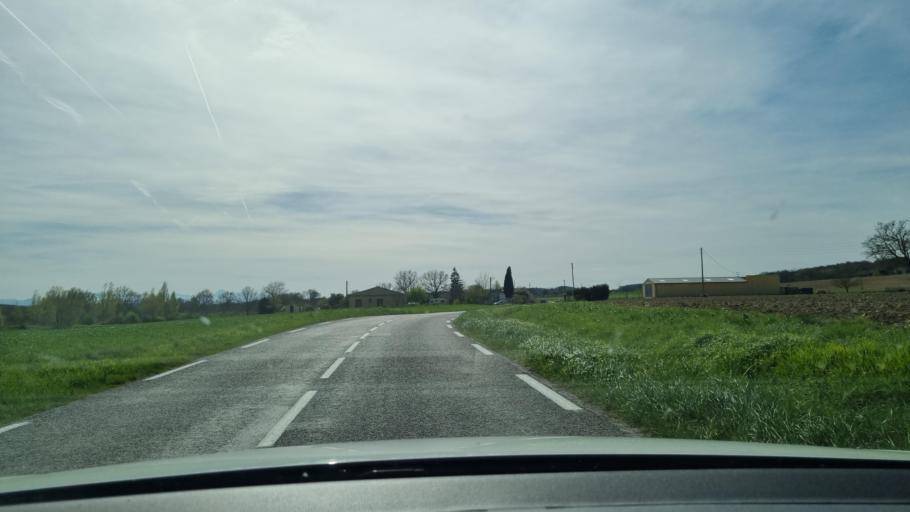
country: FR
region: Midi-Pyrenees
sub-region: Departement du Gers
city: Lombez
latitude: 43.4276
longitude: 0.8333
